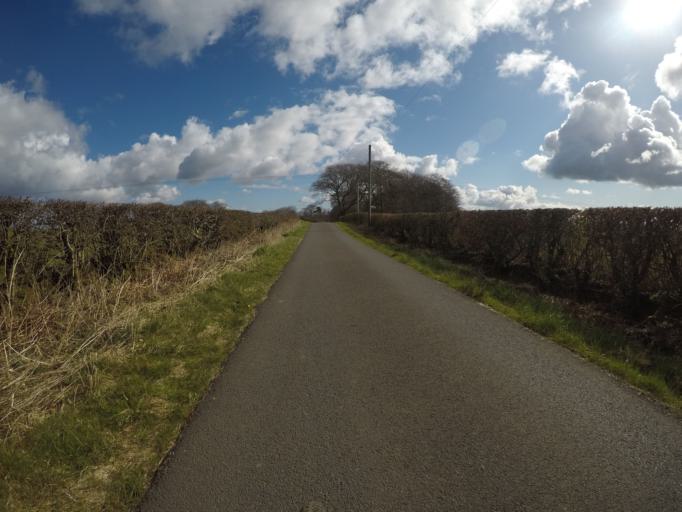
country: GB
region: Scotland
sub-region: North Ayrshire
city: Beith
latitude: 55.7126
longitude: -4.6501
